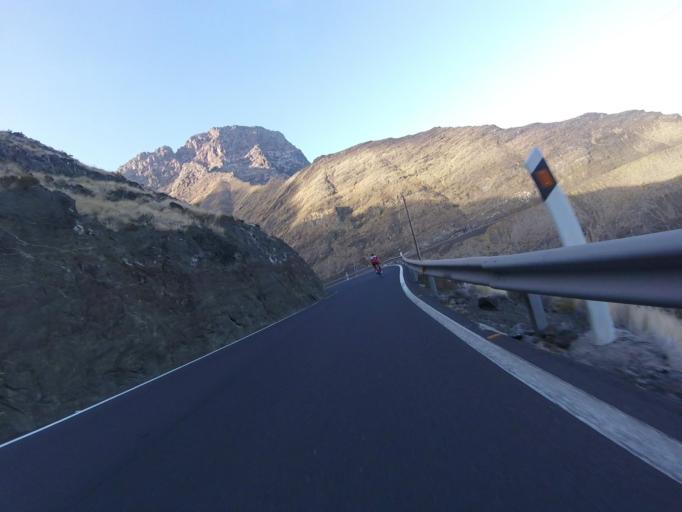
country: ES
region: Canary Islands
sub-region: Provincia de Las Palmas
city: Agaete
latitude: 28.0729
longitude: -15.7106
